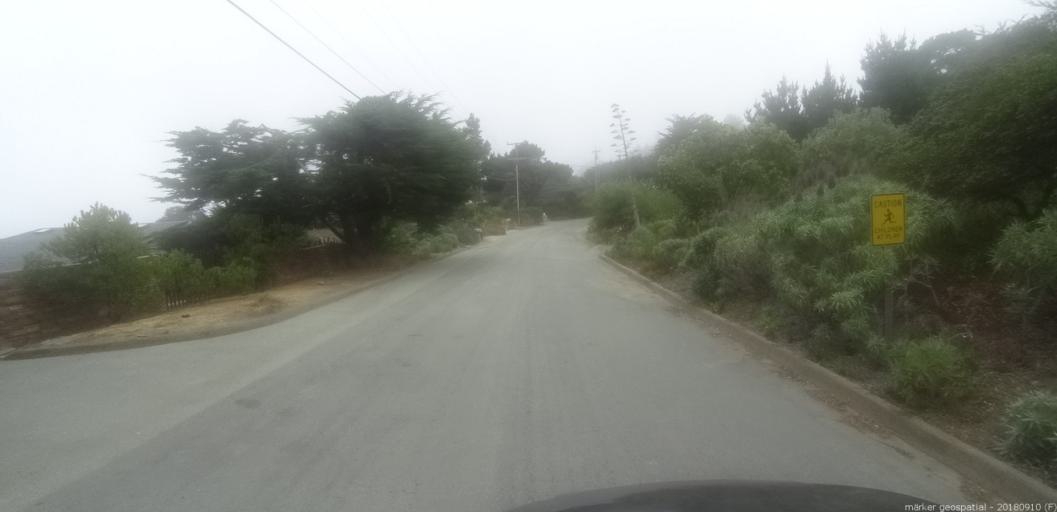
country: US
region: California
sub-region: Monterey County
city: Carmel-by-the-Sea
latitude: 36.4882
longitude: -121.9401
